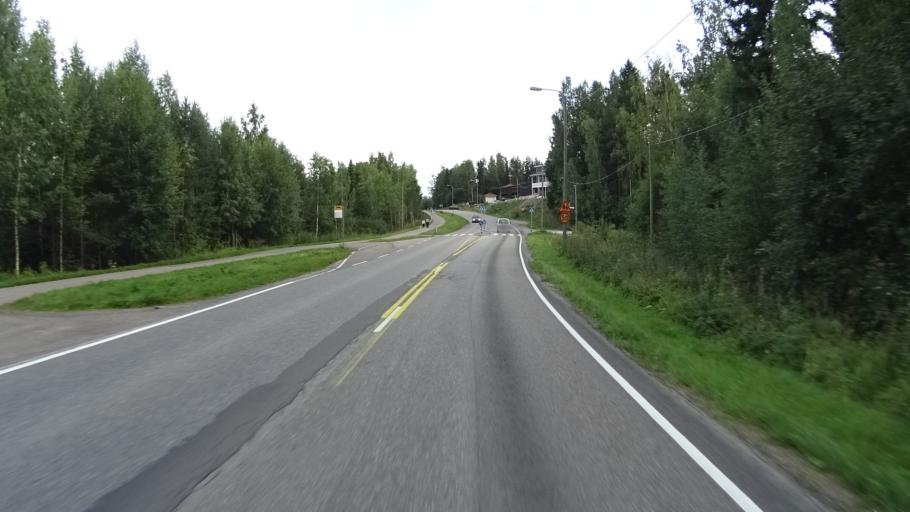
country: FI
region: Uusimaa
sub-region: Helsinki
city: Nurmijaervi
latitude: 60.3341
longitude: 24.8631
